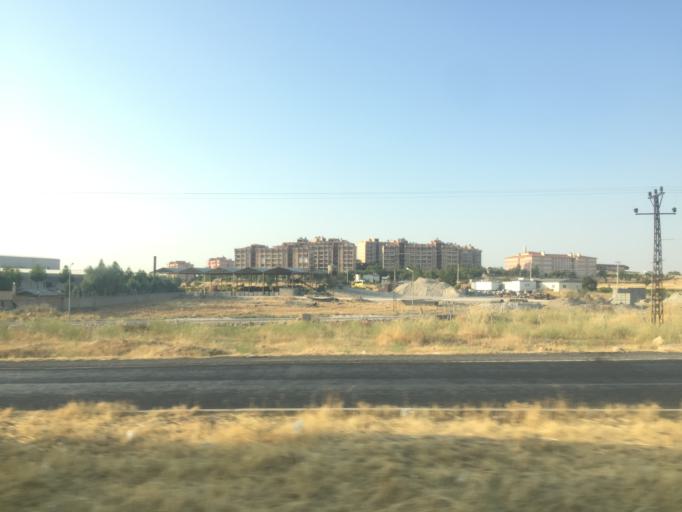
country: TR
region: Mardin
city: Midyat
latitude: 37.4367
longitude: 41.3152
